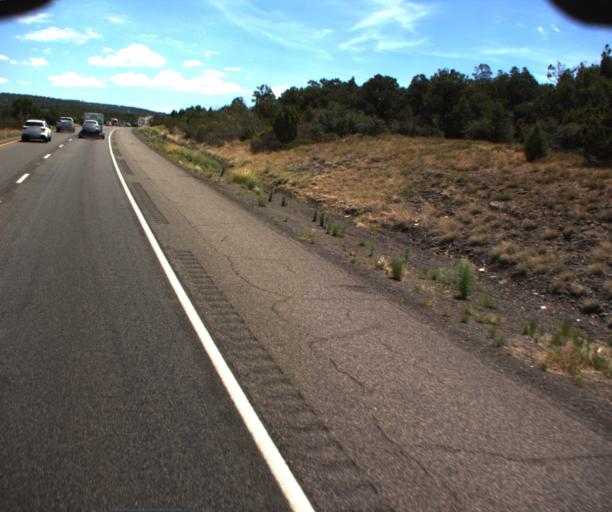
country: US
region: Arizona
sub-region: Yavapai County
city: Village of Oak Creek (Big Park)
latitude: 34.7801
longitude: -111.6183
